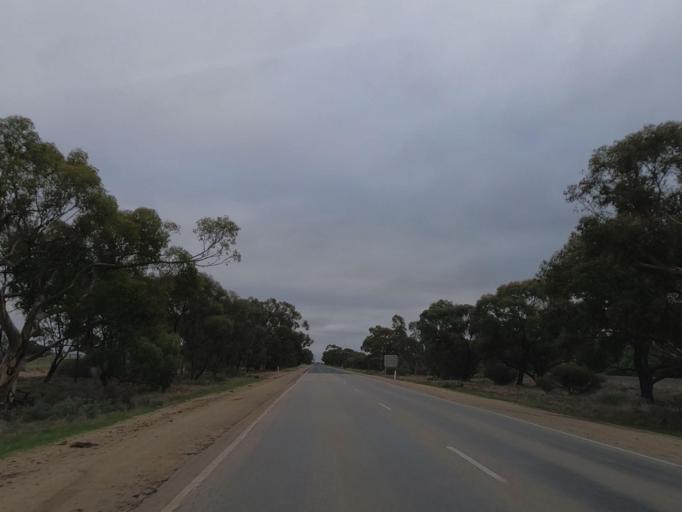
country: AU
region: Victoria
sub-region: Swan Hill
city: Swan Hill
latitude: -35.4018
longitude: 143.5780
